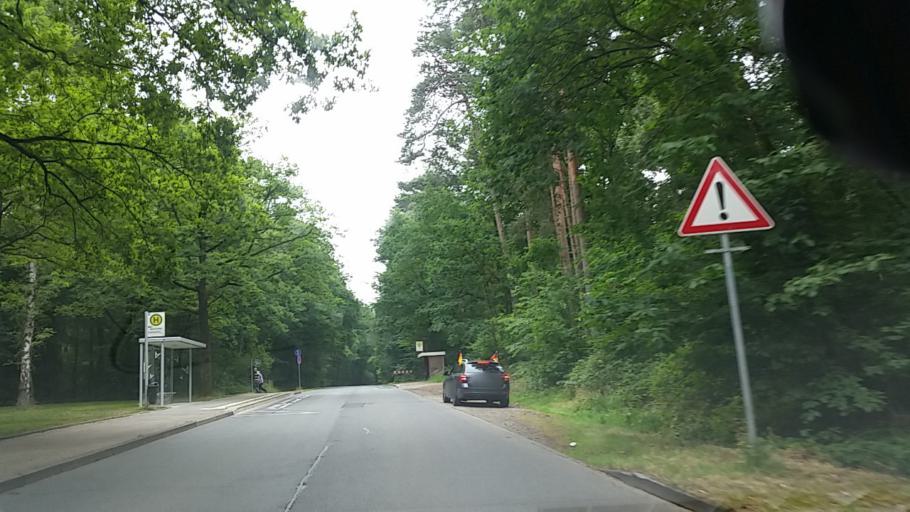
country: DE
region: Lower Saxony
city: Wolfsburg
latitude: 52.4606
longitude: 10.8016
